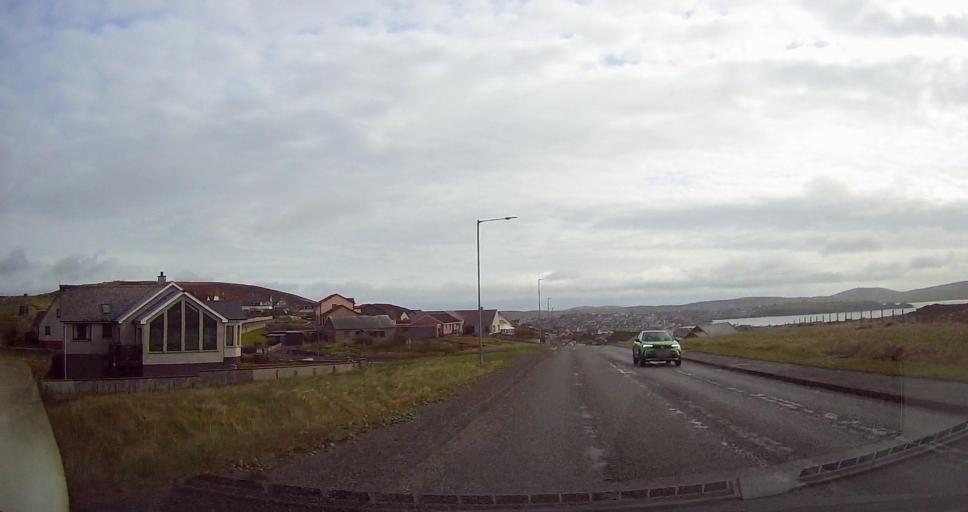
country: GB
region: Scotland
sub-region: Shetland Islands
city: Lerwick
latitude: 60.1414
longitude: -1.1847
